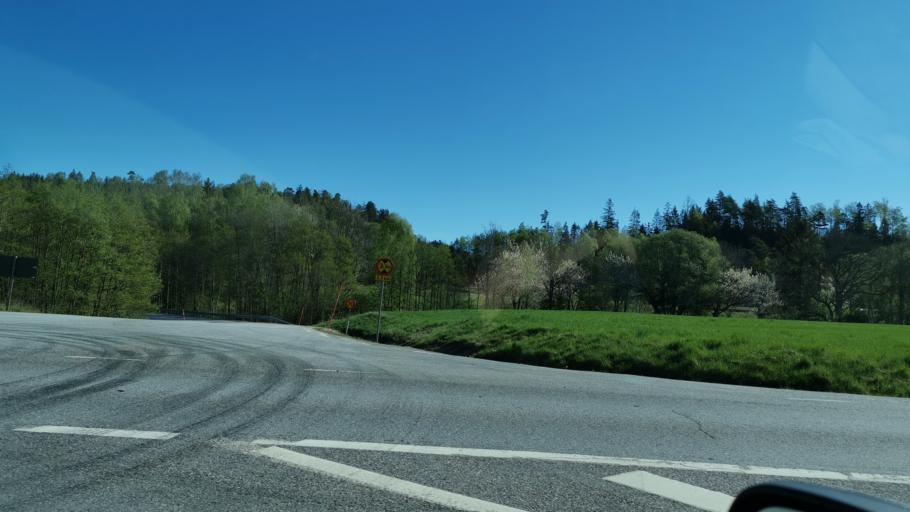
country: SE
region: Vaestra Goetaland
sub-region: Uddevalla Kommun
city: Ljungskile
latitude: 58.2617
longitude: 11.9012
